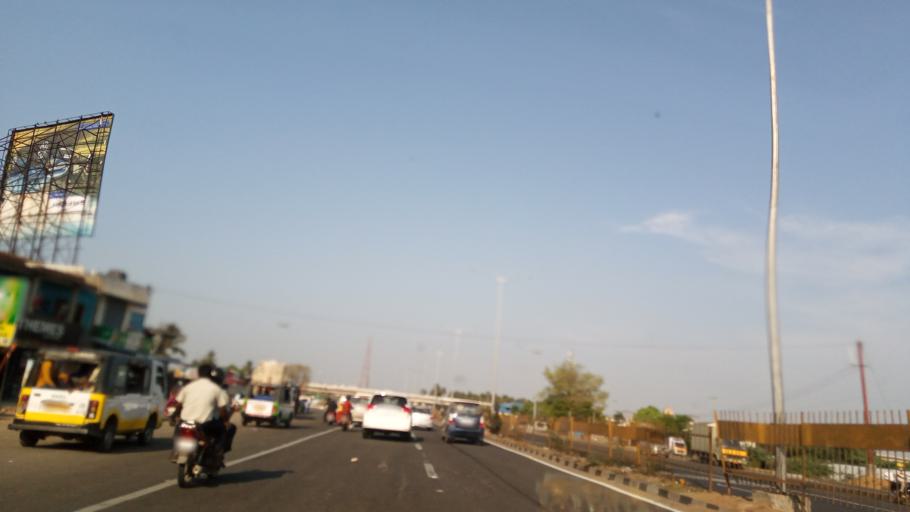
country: IN
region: Tamil Nadu
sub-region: Kancheepuram
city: Poonamalle
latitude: 13.0473
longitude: 80.0805
